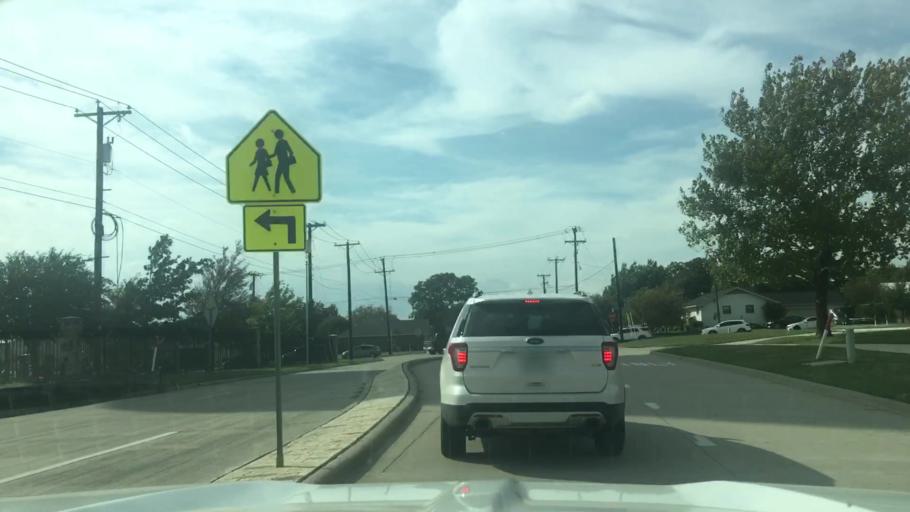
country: US
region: Texas
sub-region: Collin County
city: Prosper
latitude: 33.2336
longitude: -96.7925
